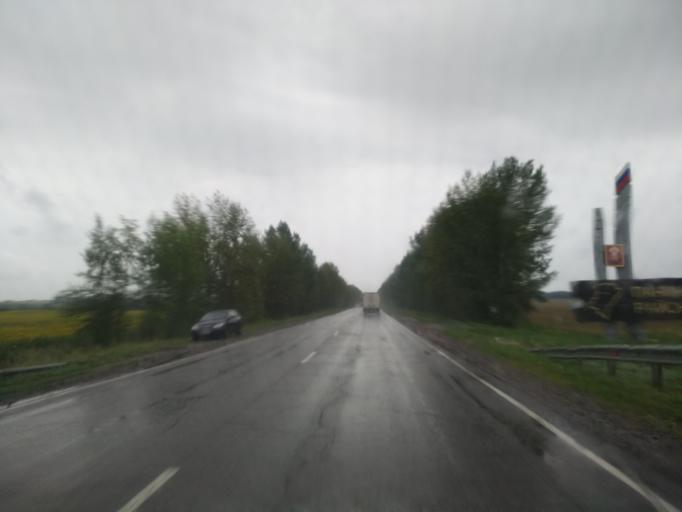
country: RU
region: Voronezj
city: Verkhnyaya Khava
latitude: 51.6818
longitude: 39.9014
